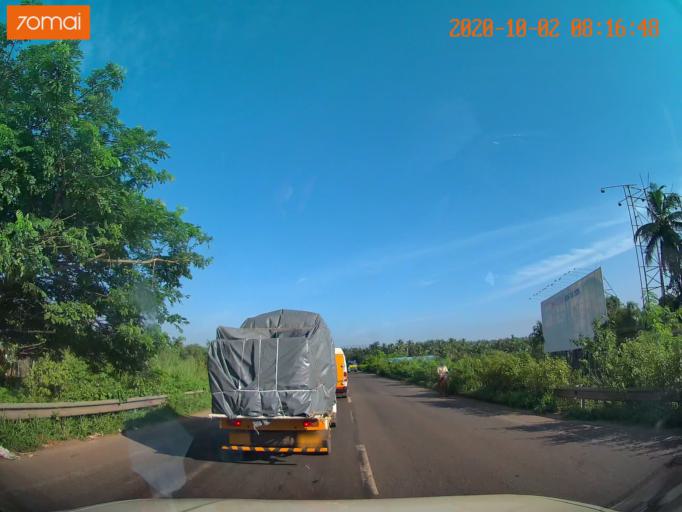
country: IN
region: Kerala
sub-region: Kozhikode
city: Kozhikode
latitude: 11.2951
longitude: 75.7970
